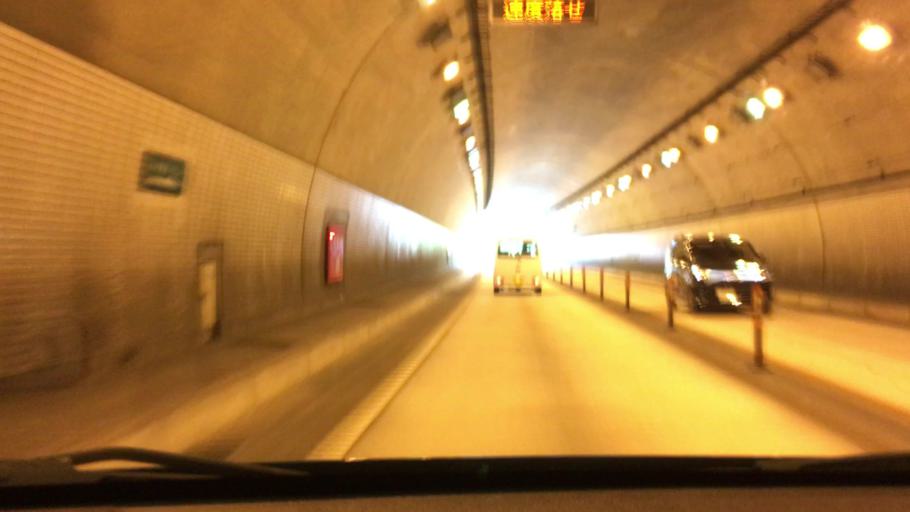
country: JP
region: Nagasaki
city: Sasebo
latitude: 33.1008
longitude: 129.7794
